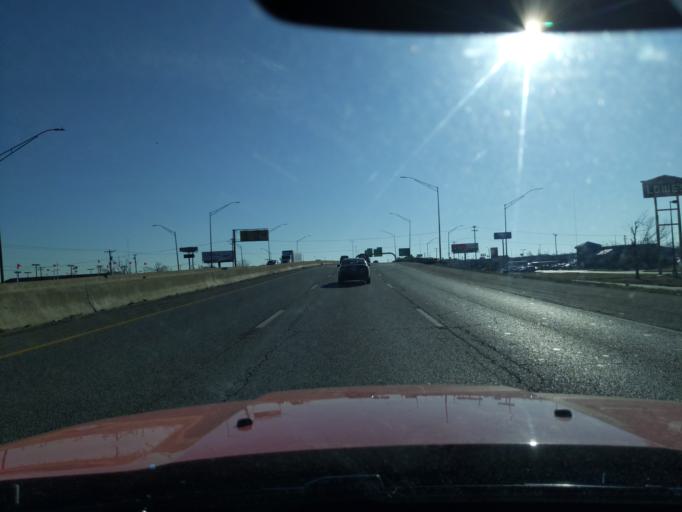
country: US
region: Oklahoma
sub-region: Cleveland County
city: Moore
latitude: 35.3919
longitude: -97.5151
